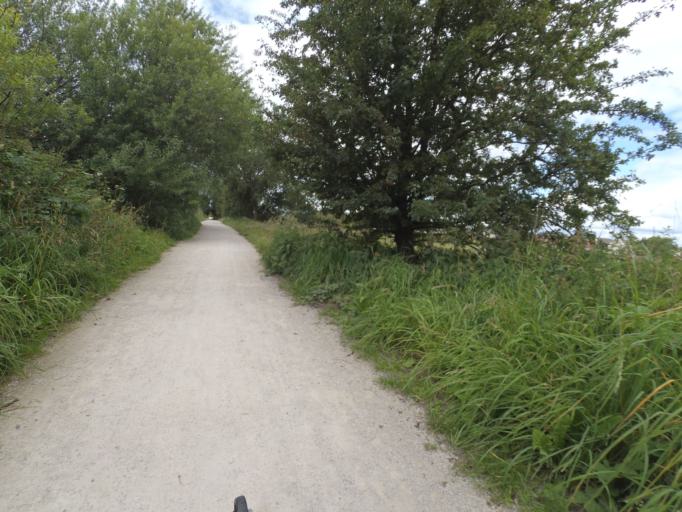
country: GB
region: England
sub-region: Staffordshire
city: Stafford
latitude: 52.8077
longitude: -2.1415
